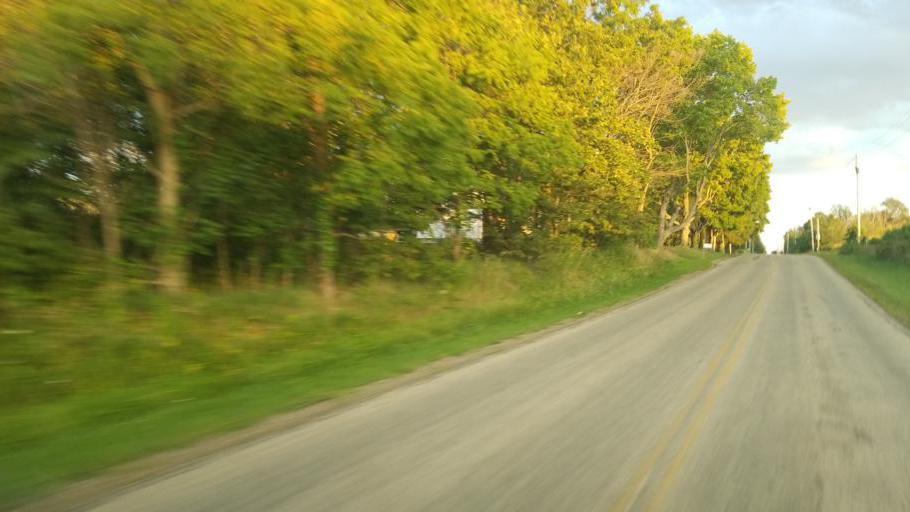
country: US
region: Ohio
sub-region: Richland County
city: Mansfield
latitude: 40.8119
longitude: -82.5431
